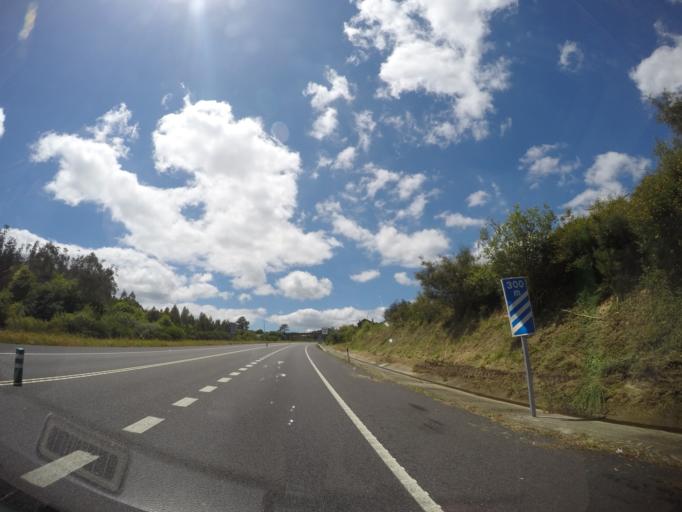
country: ES
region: Galicia
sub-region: Provincia da Coruna
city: Noia
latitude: 42.7626
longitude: -8.9415
